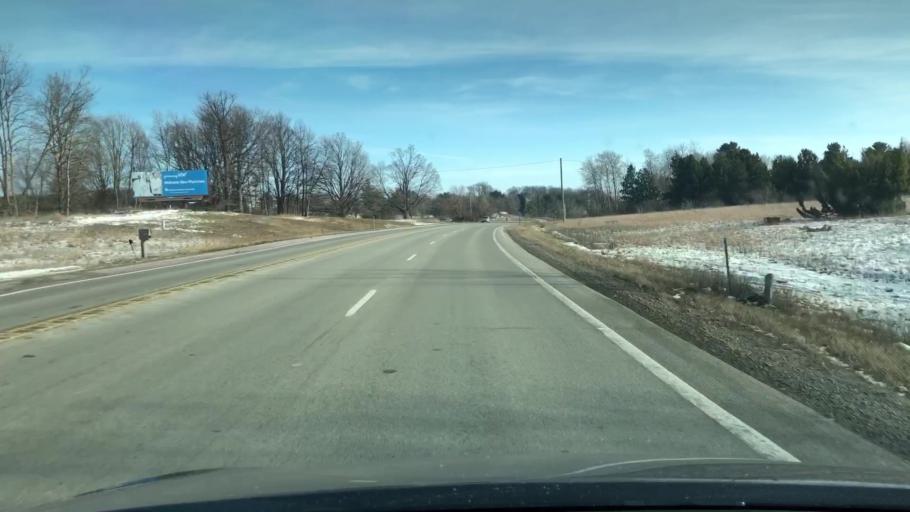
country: US
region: Michigan
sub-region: Kalkaska County
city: Rapid City
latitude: 44.7794
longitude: -85.3510
